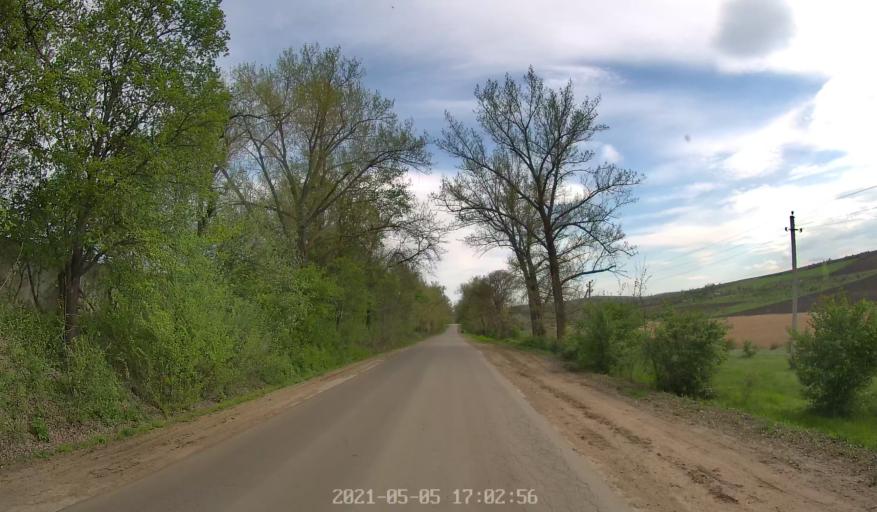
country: MD
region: Chisinau
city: Vadul lui Voda
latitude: 47.0558
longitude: 29.1325
